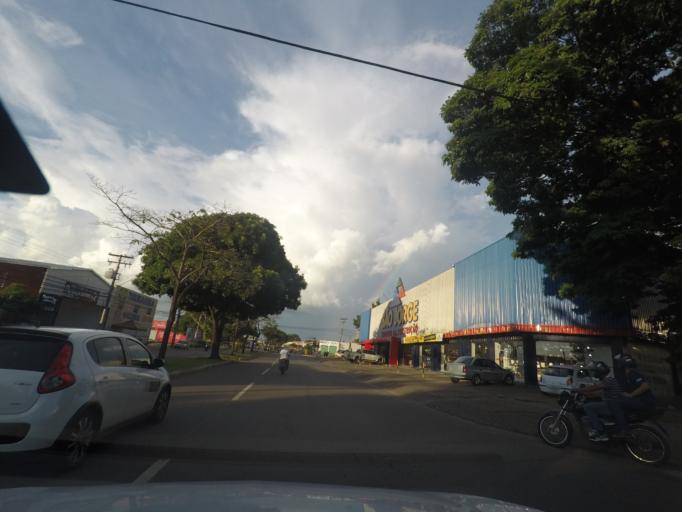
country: BR
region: Goias
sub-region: Goiania
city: Goiania
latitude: -16.6689
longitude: -49.3125
